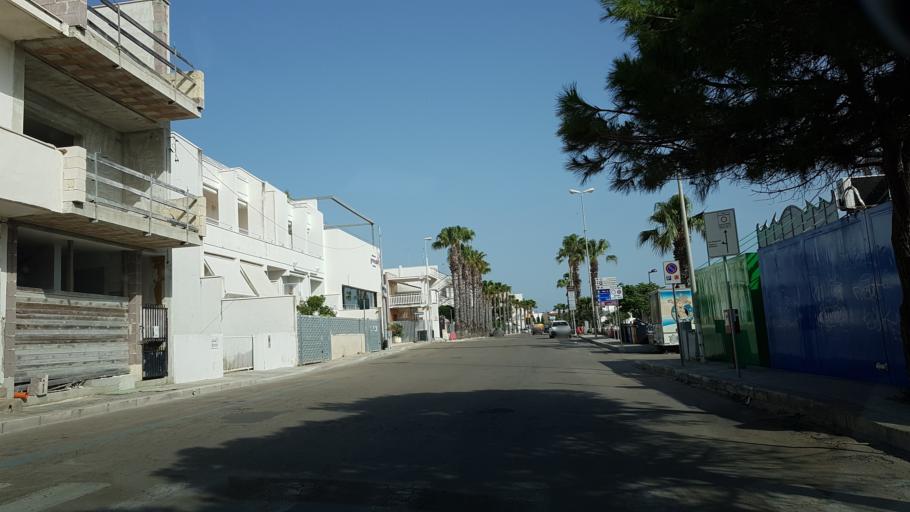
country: IT
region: Apulia
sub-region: Provincia di Lecce
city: Porto Cesareo
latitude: 40.2621
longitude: 17.8889
